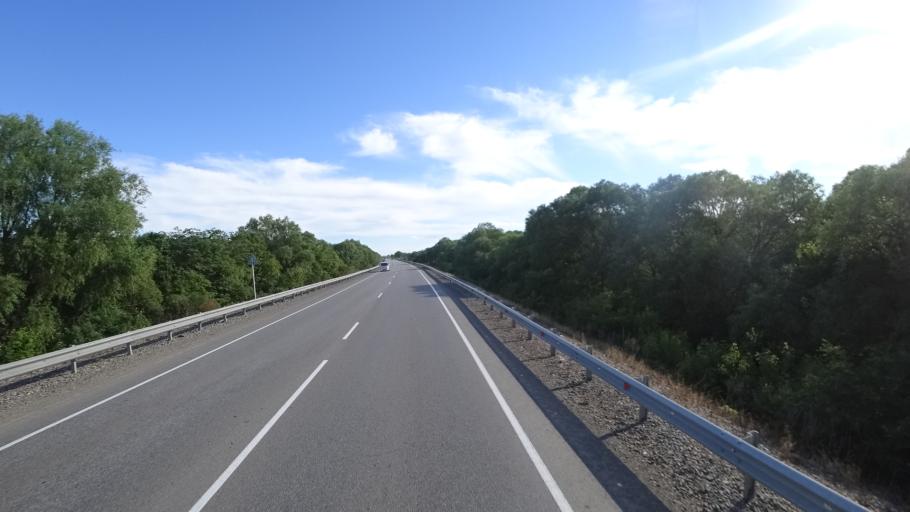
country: RU
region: Khabarovsk Krai
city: Khor
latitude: 47.8819
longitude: 134.9713
